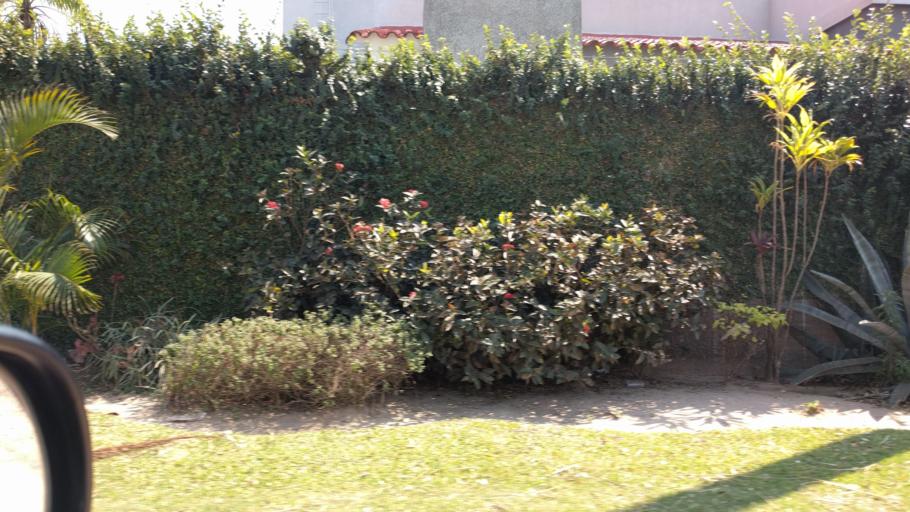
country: BO
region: Santa Cruz
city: Santa Cruz de la Sierra
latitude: -17.7537
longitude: -63.2236
